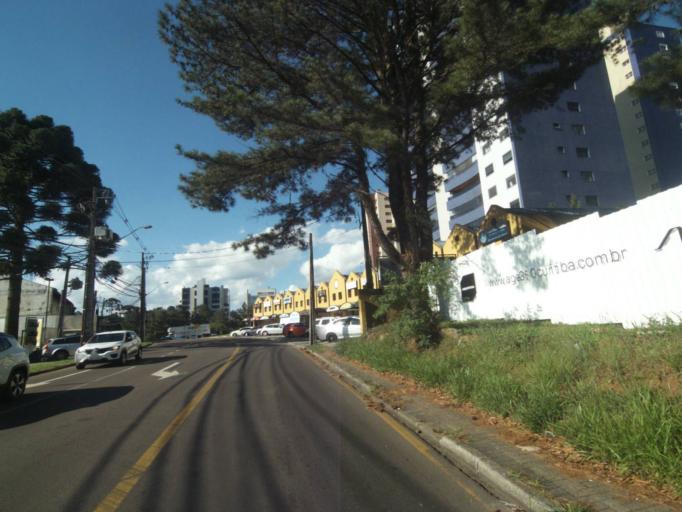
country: BR
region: Parana
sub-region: Curitiba
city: Curitiba
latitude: -25.4387
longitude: -49.3220
